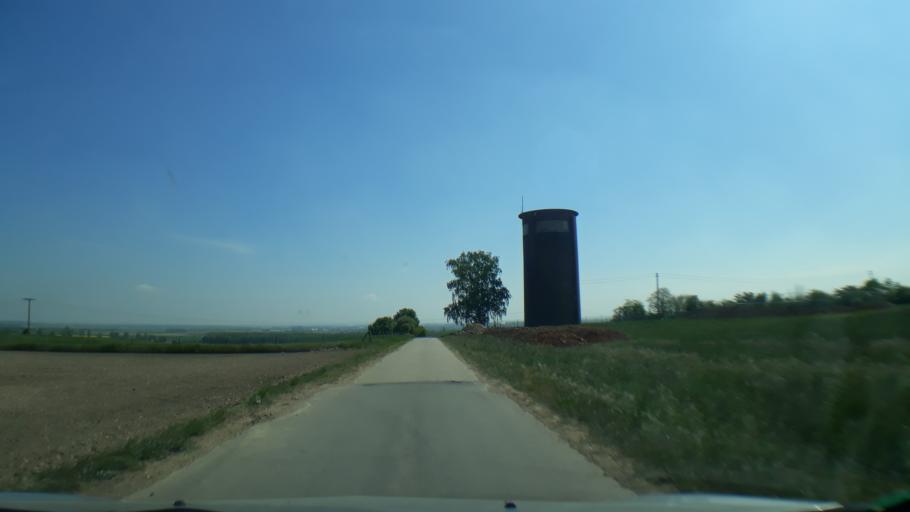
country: DE
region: North Rhine-Westphalia
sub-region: Regierungsbezirk Koln
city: Vettweiss
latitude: 50.7042
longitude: 6.5690
